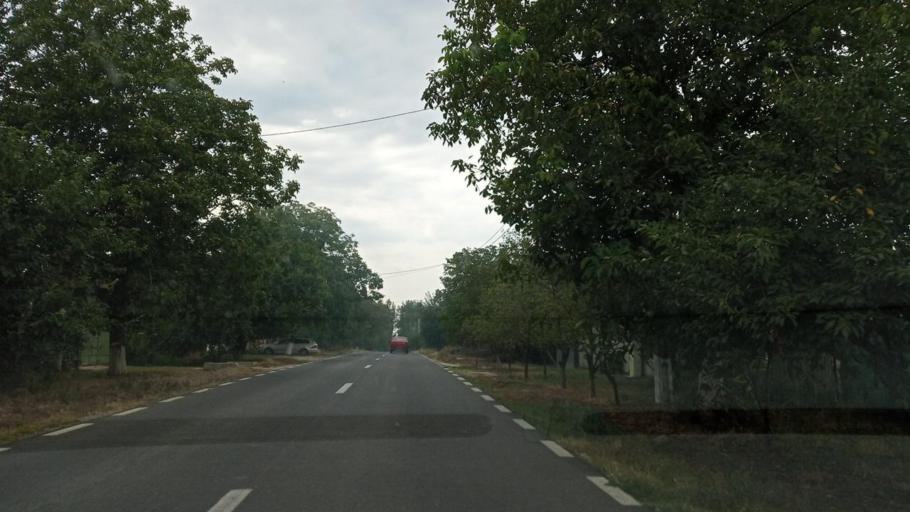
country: RO
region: Giurgiu
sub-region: Comuna Gostinari
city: Gostinari
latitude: 44.1728
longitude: 26.2397
